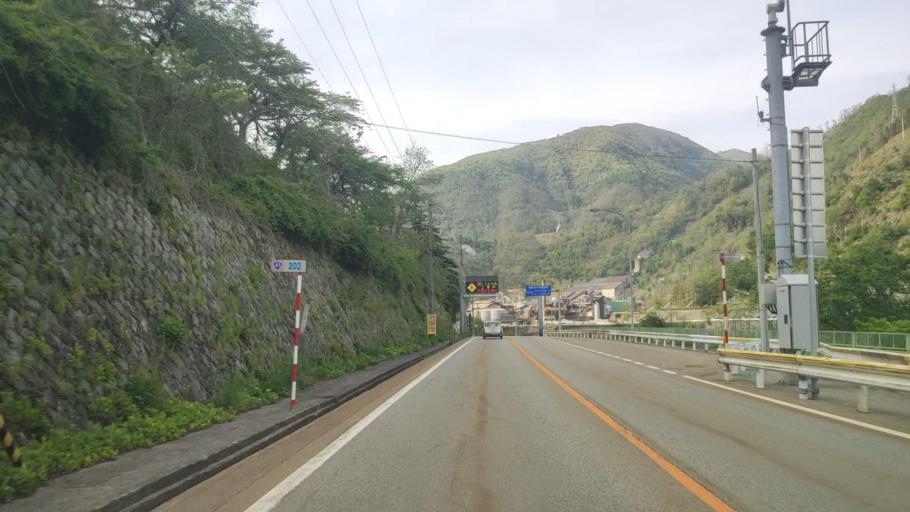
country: JP
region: Gifu
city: Takayama
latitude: 36.3418
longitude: 137.2949
